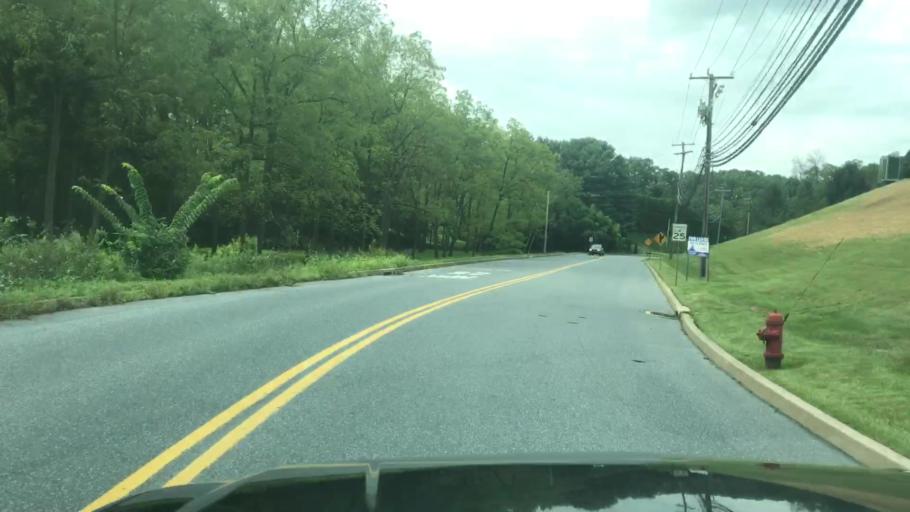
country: US
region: Pennsylvania
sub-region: Dauphin County
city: Progress
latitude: 40.3071
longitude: -76.8456
